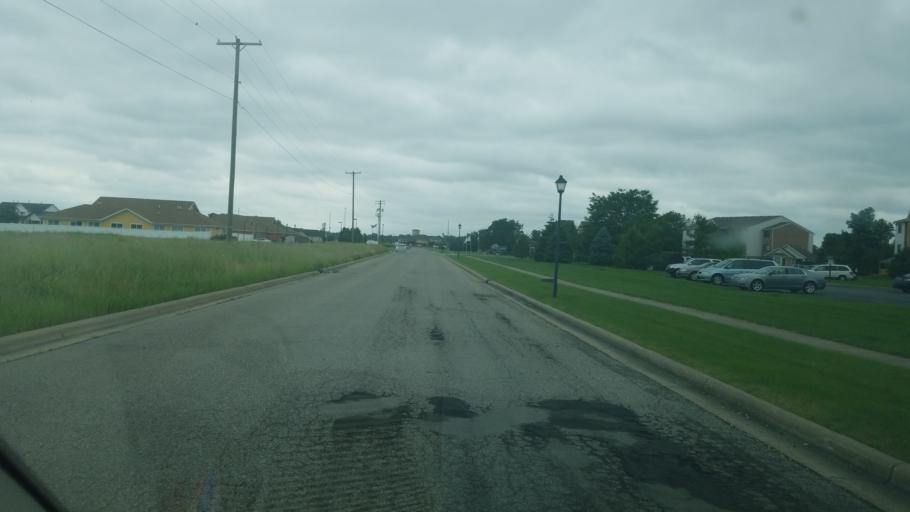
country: US
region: Ohio
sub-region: Marion County
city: Marion
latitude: 40.5689
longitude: -83.1158
